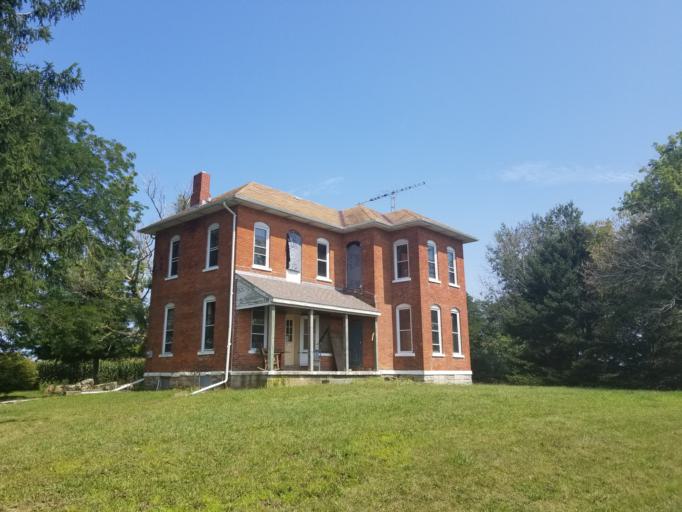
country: US
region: Ohio
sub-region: Crawford County
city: Bucyrus
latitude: 40.8503
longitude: -83.1087
